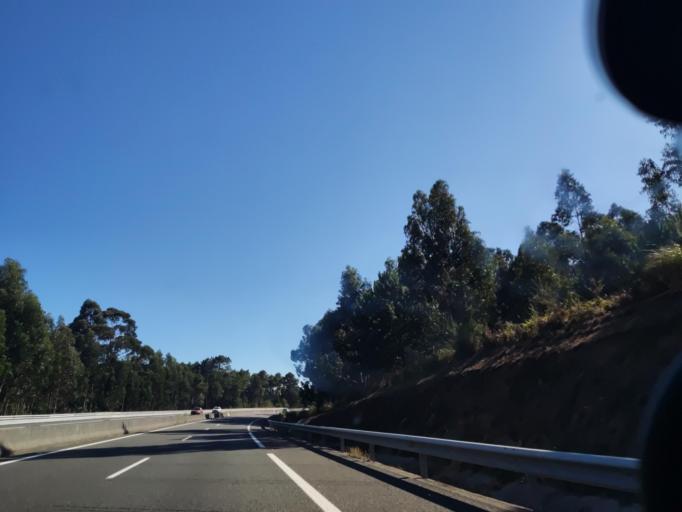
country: ES
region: Galicia
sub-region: Provincia da Coruna
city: Boiro
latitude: 42.5795
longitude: -8.9886
